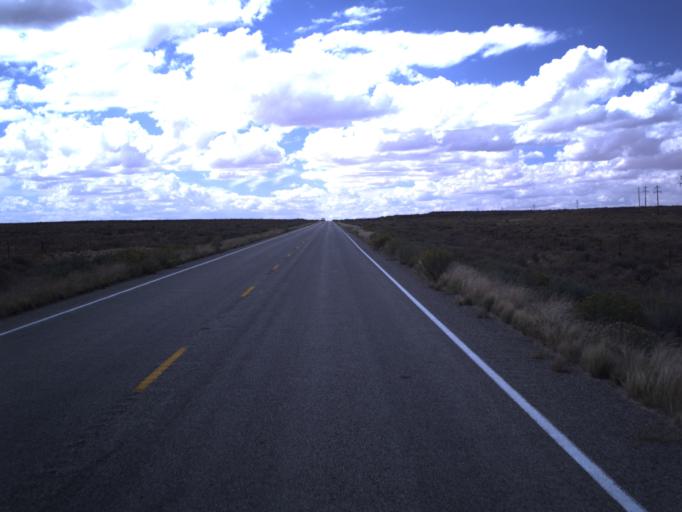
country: US
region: Utah
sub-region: San Juan County
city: Blanding
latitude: 37.2718
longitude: -109.7166
